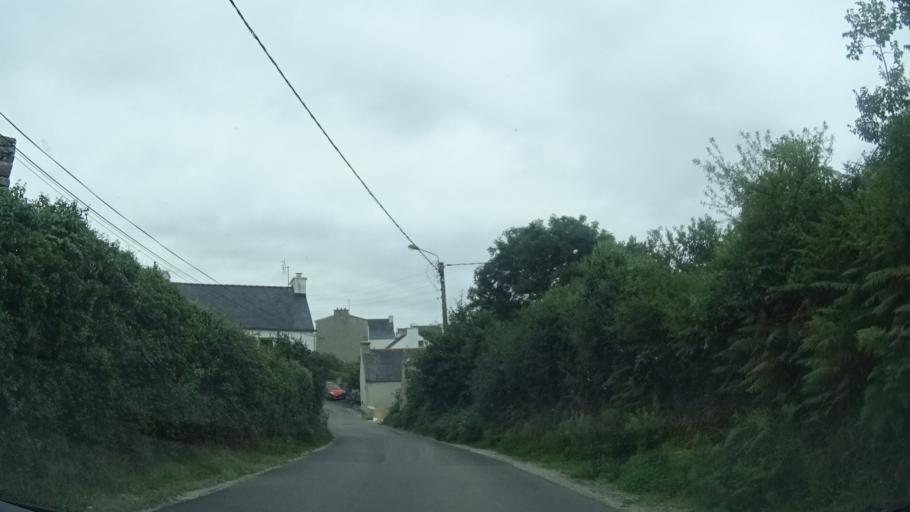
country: FR
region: Brittany
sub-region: Departement du Finistere
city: Lampaul-Plouarzel
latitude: 48.4508
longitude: -4.7601
